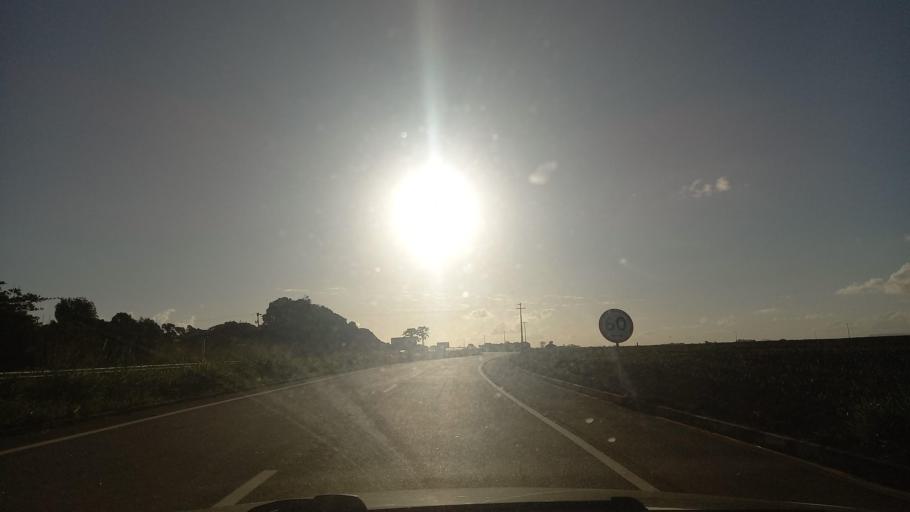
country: BR
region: Alagoas
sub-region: Campo Alegre
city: Campo Alegre
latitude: -9.7886
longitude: -36.3272
